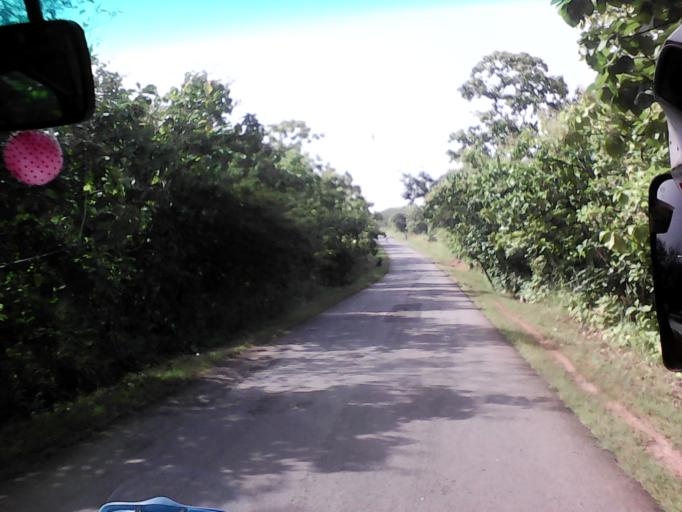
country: TG
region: Centrale
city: Sokode
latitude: 9.1300
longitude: 1.1479
